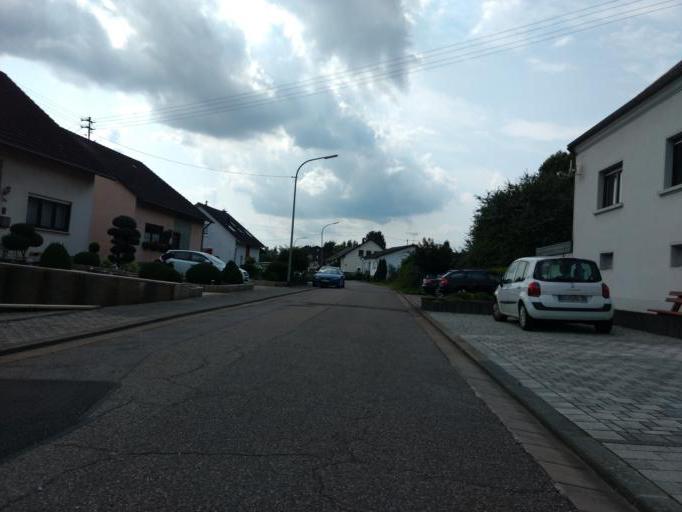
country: DE
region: Saarland
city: Nalbach
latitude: 49.3933
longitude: 6.8247
